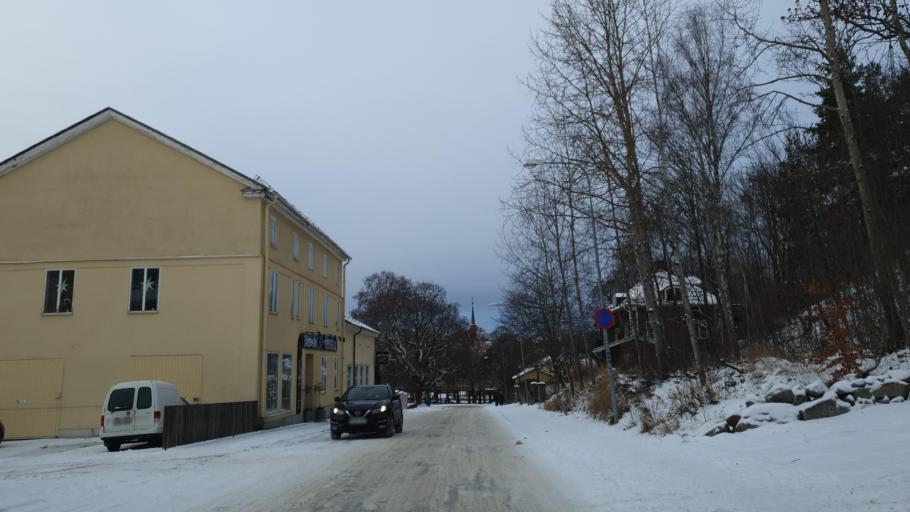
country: SE
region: Gaevleborg
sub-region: Soderhamns Kommun
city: Soderhamn
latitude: 61.2999
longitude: 17.0560
